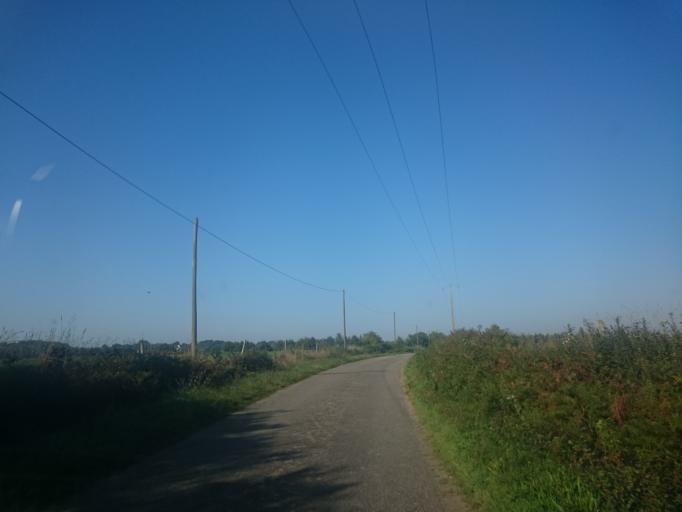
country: FR
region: Brittany
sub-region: Departement d'Ille-et-Vilaine
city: Corps-Nuds
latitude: 47.9312
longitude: -1.5758
